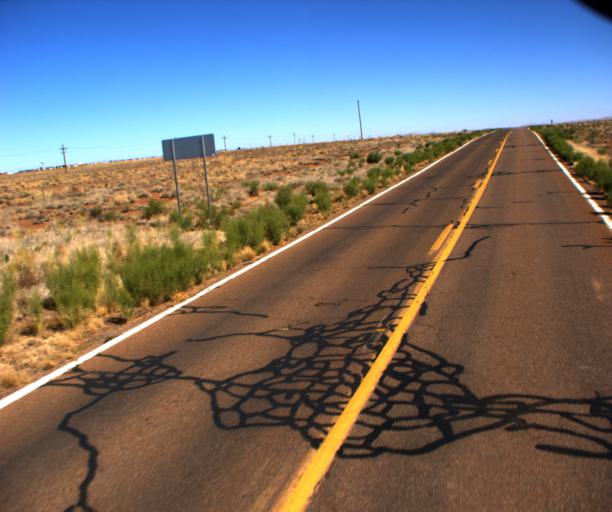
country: US
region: Arizona
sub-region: Coconino County
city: LeChee
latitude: 35.2833
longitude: -110.9829
